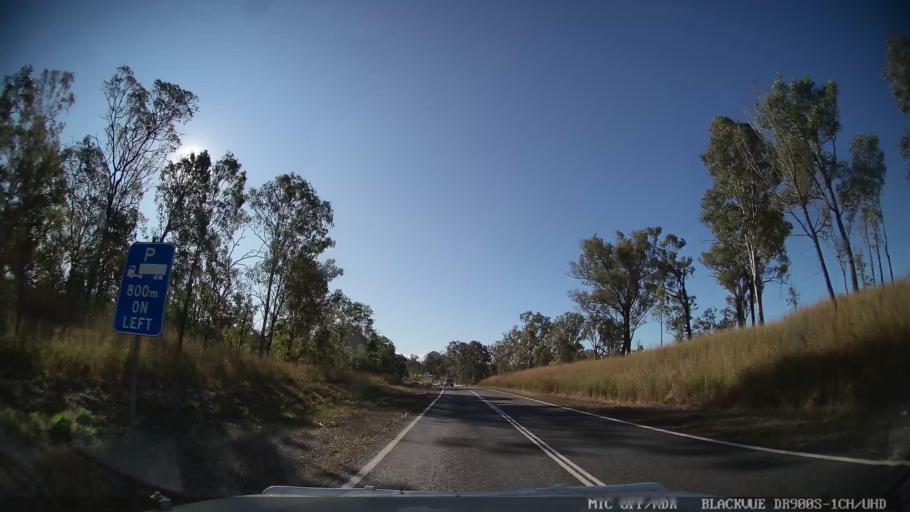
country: AU
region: Queensland
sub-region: Bundaberg
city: Sharon
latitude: -24.8310
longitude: 151.7089
